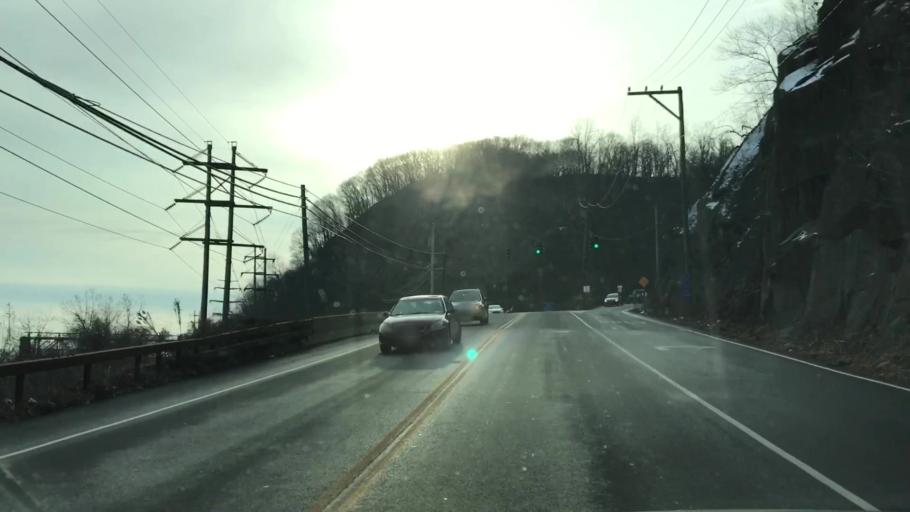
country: US
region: New York
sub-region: Rockland County
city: Haverstraw
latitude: 41.1830
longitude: -73.9557
